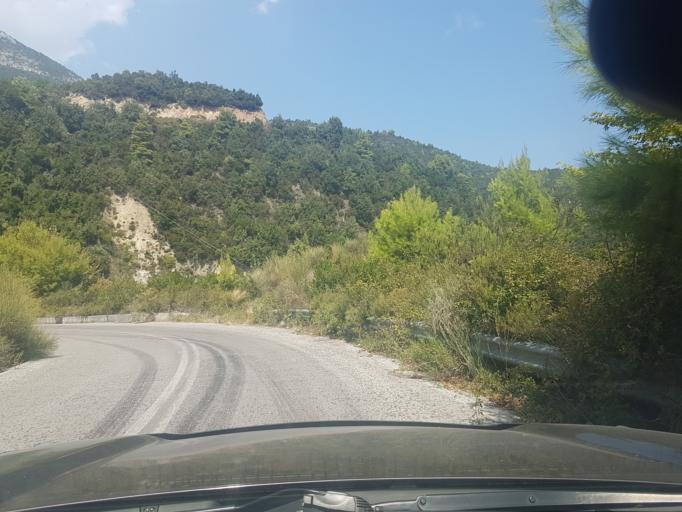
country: GR
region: Central Greece
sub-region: Nomos Evvoias
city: Kymi
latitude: 38.6533
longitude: 23.9226
